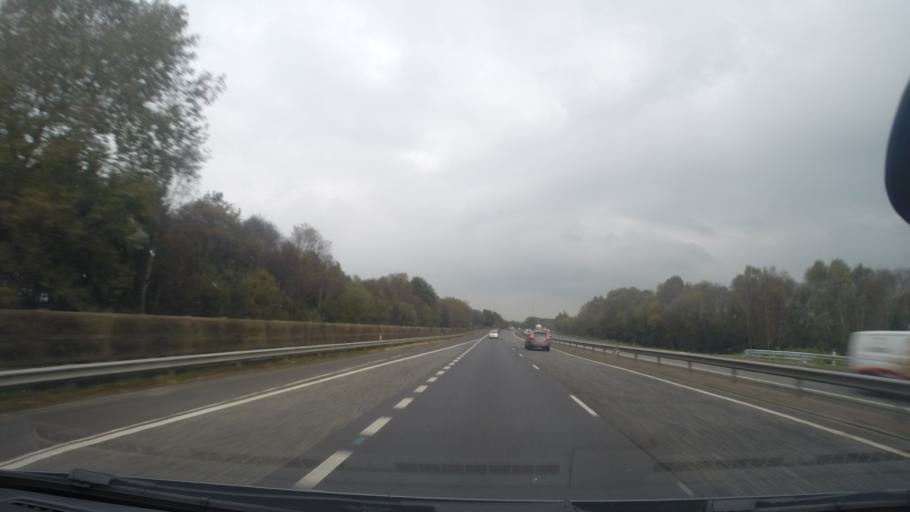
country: GB
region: Northern Ireland
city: Moy
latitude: 54.4824
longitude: -6.6145
